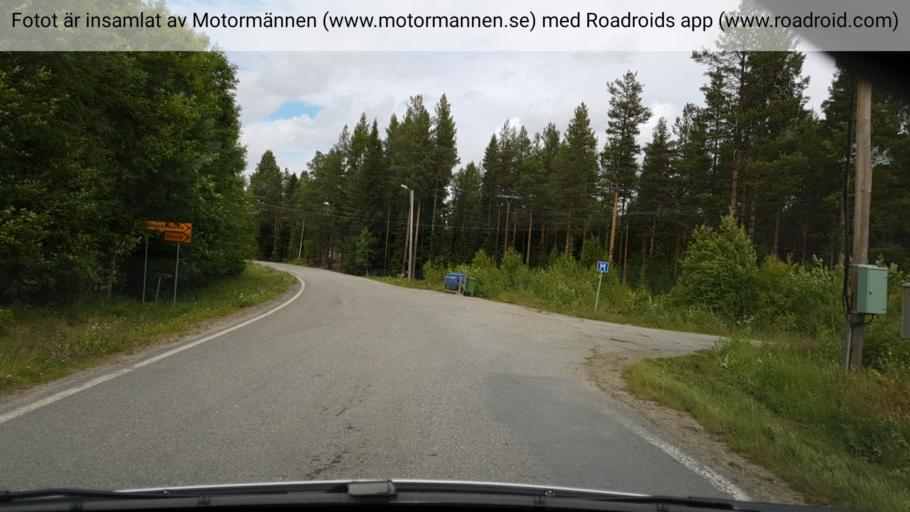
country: SE
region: Vaesternorrland
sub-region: Solleftea Kommun
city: As
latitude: 63.7952
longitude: 16.6995
